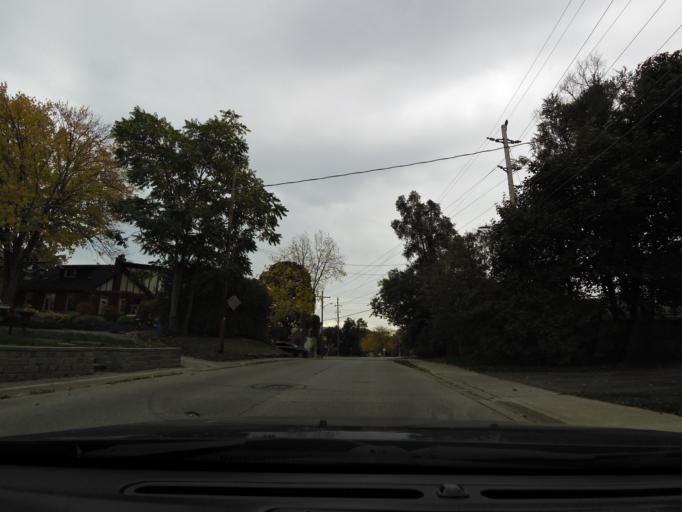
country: CA
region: Ontario
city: Hamilton
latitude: 43.2987
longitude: -79.8646
